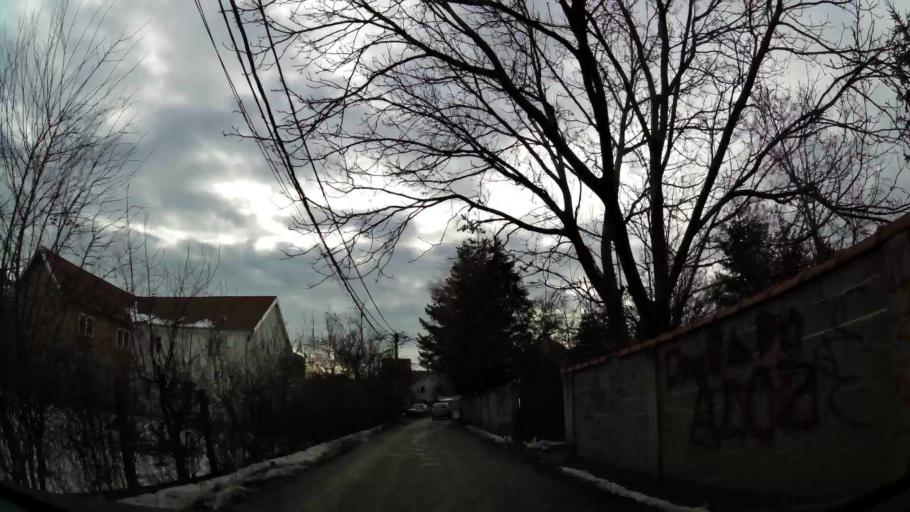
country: RS
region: Central Serbia
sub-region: Belgrade
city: Surcin
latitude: 44.8017
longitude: 20.3351
